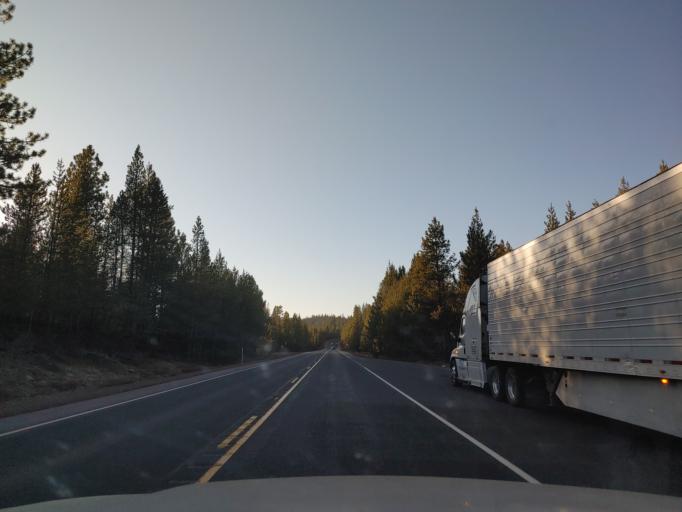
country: US
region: Oregon
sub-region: Deschutes County
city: La Pine
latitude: 43.4394
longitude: -121.8639
